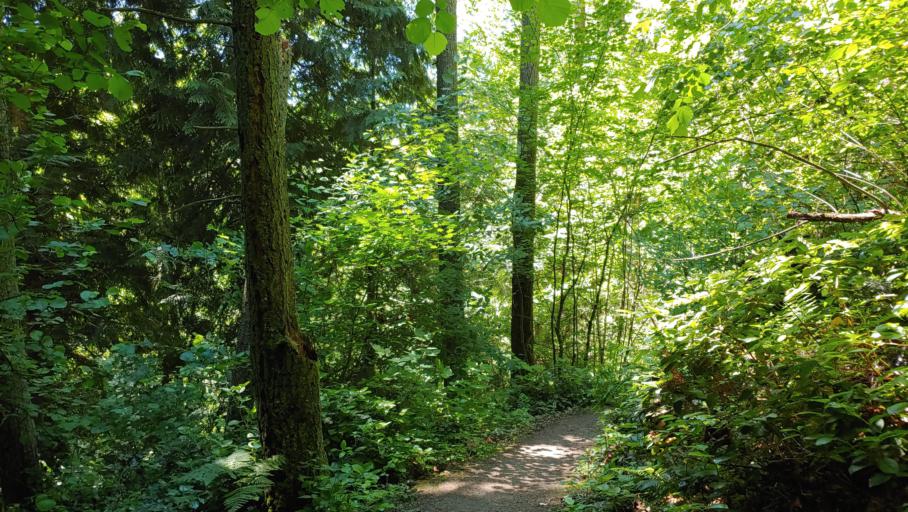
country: US
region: Washington
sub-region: King County
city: Newcastle
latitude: 47.5175
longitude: -122.1835
